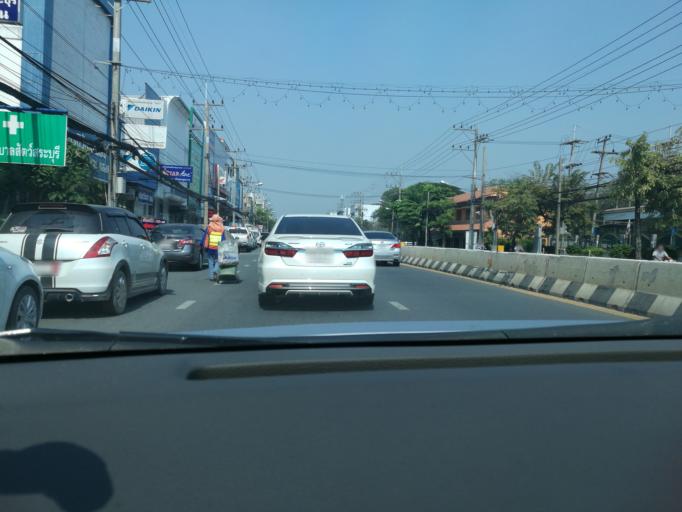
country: TH
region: Sara Buri
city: Saraburi
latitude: 14.5348
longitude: 100.9112
